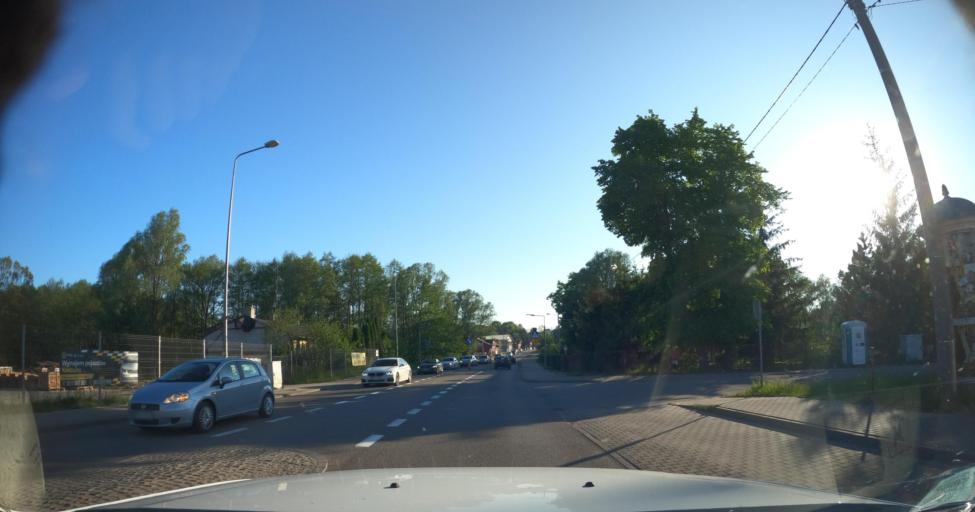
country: PL
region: Pomeranian Voivodeship
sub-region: Powiat kartuski
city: Zukowo
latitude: 54.3414
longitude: 18.3552
